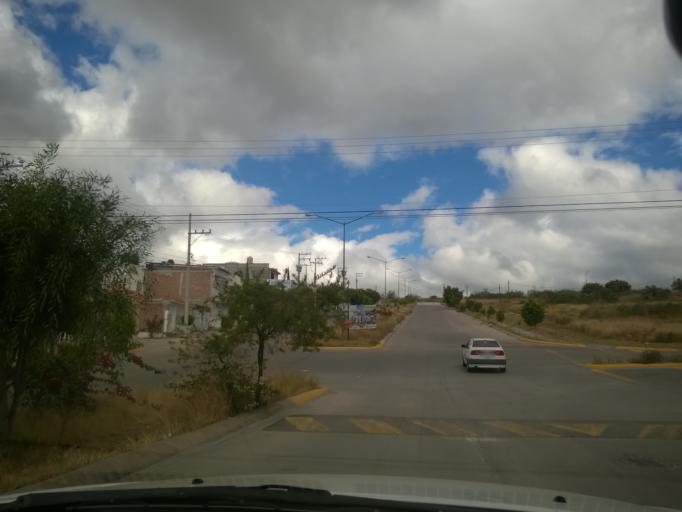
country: MX
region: Guanajuato
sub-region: Leon
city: La Ermita
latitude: 21.1582
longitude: -101.7371
